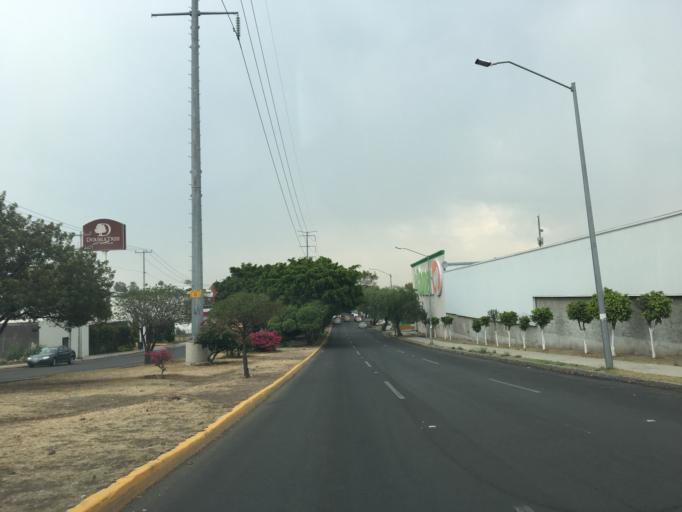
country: MX
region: Queretaro
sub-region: Queretaro
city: Santiago de Queretaro
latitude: 20.5780
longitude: -100.3721
